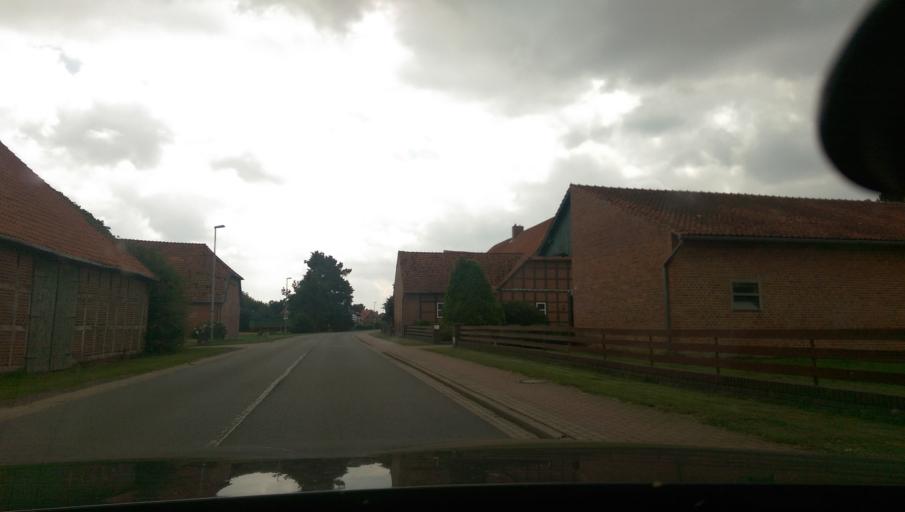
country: DE
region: Lower Saxony
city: Frankenfeld
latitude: 52.6884
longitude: 9.4825
